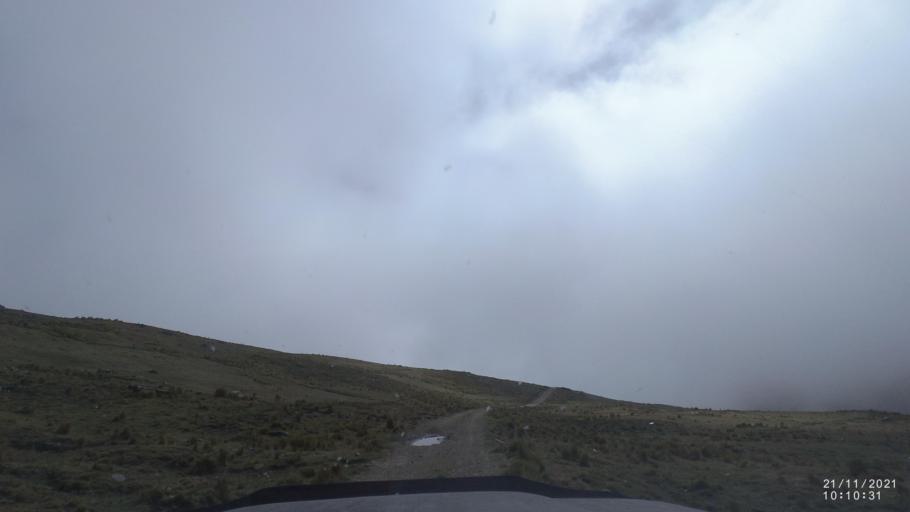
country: BO
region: Cochabamba
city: Cochabamba
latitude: -16.9957
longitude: -66.2738
